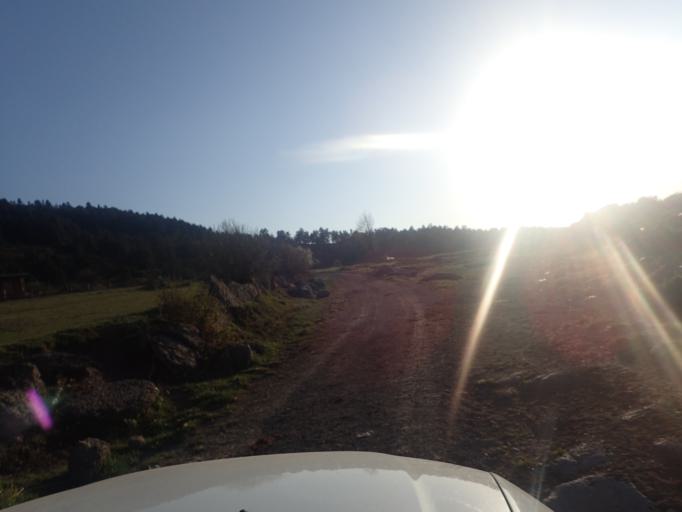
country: TR
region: Sivas
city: Koyulhisar
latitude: 40.3575
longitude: 37.8467
